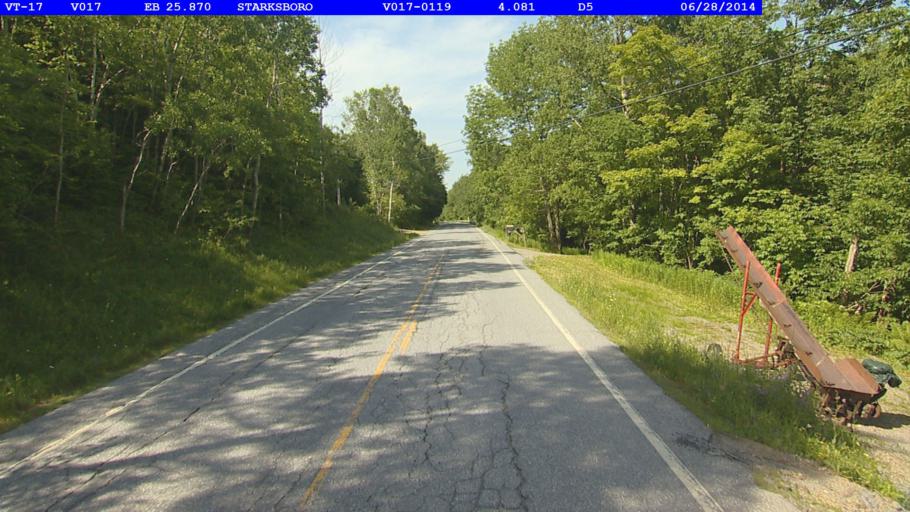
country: US
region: Vermont
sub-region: Addison County
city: Bristol
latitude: 44.1979
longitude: -72.9652
